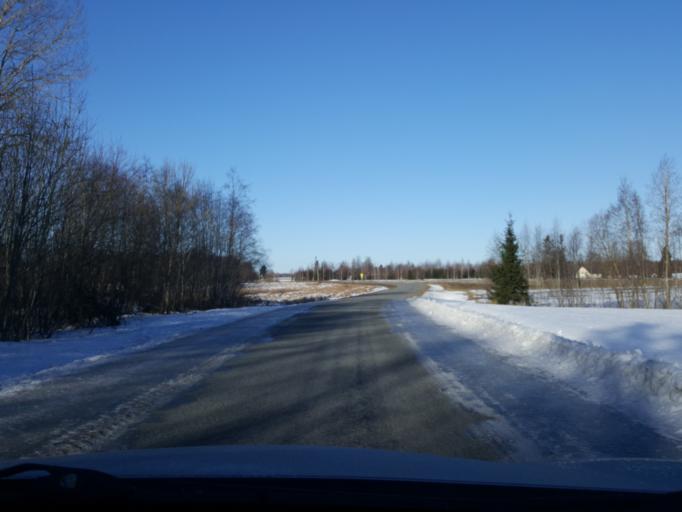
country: EE
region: Viljandimaa
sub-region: Viljandi linn
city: Viljandi
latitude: 58.4058
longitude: 25.5701
